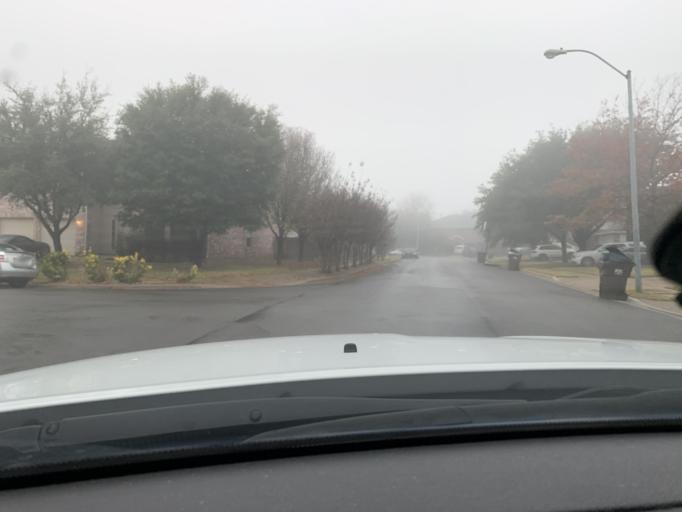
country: US
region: Texas
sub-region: Williamson County
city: Round Rock
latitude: 30.5646
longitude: -97.6652
